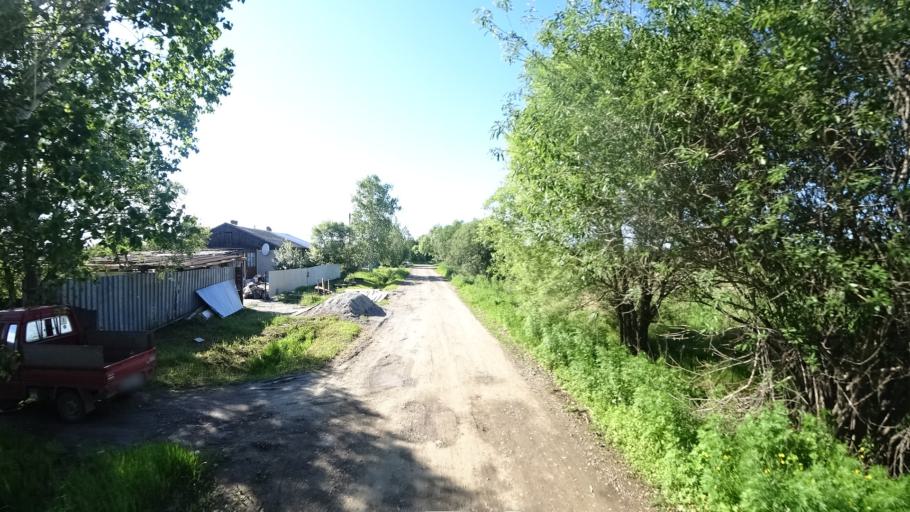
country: RU
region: Khabarovsk Krai
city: Khor
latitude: 47.8946
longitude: 134.9958
